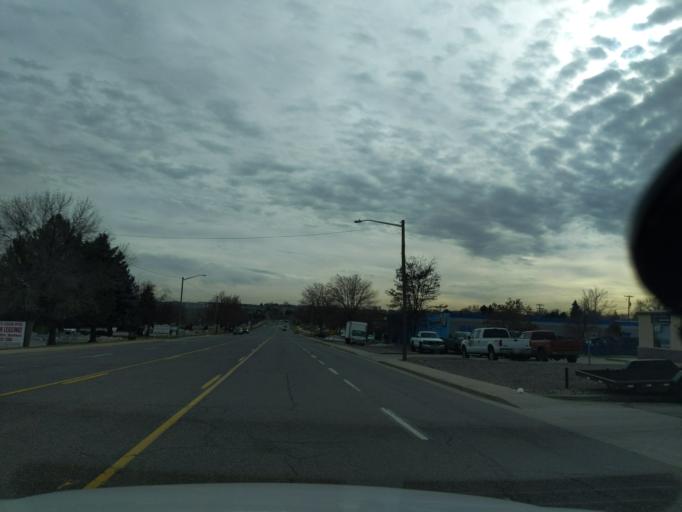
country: US
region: Colorado
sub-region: Adams County
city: Northglenn
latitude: 39.8924
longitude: -104.9658
